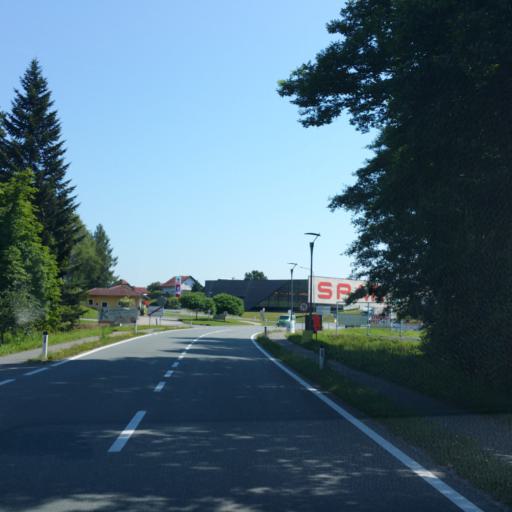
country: AT
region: Styria
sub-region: Politischer Bezirk Leibnitz
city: Gleinstatten
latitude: 46.7559
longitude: 15.3701
